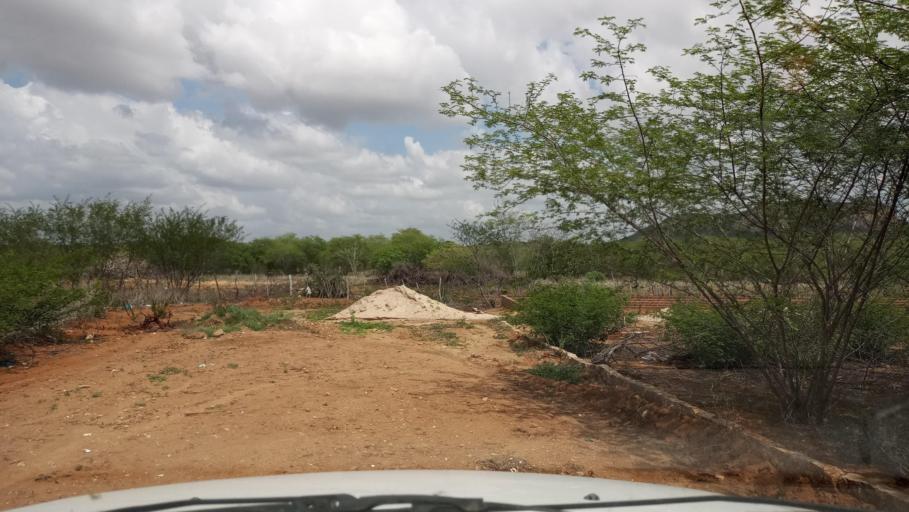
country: BR
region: Rio Grande do Norte
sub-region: Tangara
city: Tangara
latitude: -6.1120
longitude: -35.7173
